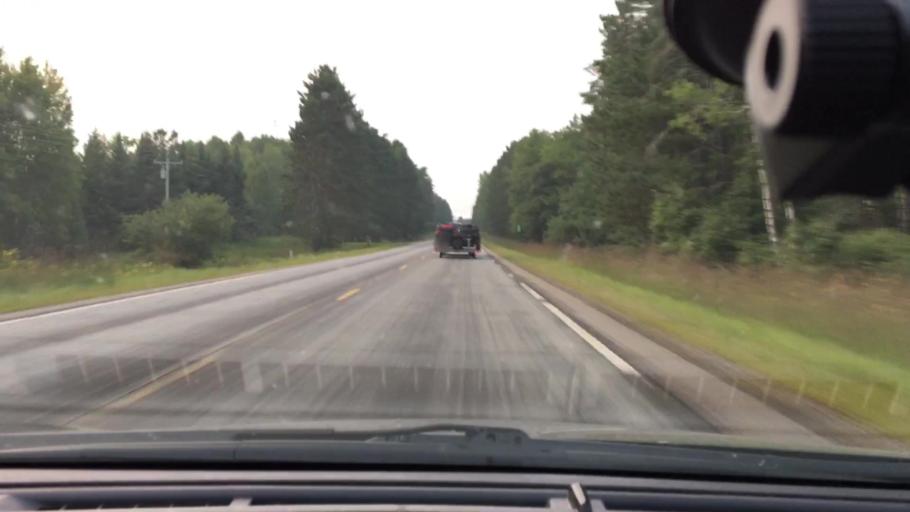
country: US
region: Minnesota
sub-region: Crow Wing County
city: Cross Lake
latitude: 46.7461
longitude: -93.9668
